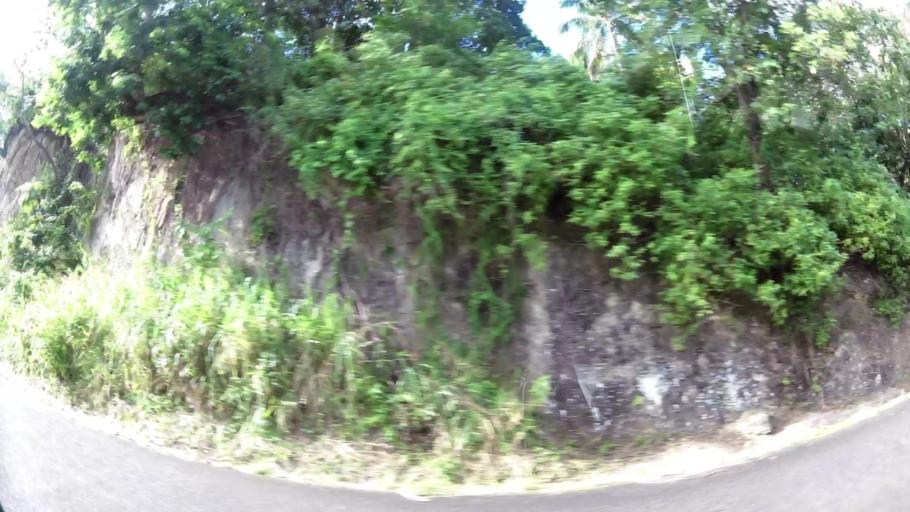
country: LC
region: Anse-la-Raye
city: Canaries
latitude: 13.8972
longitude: -61.0602
